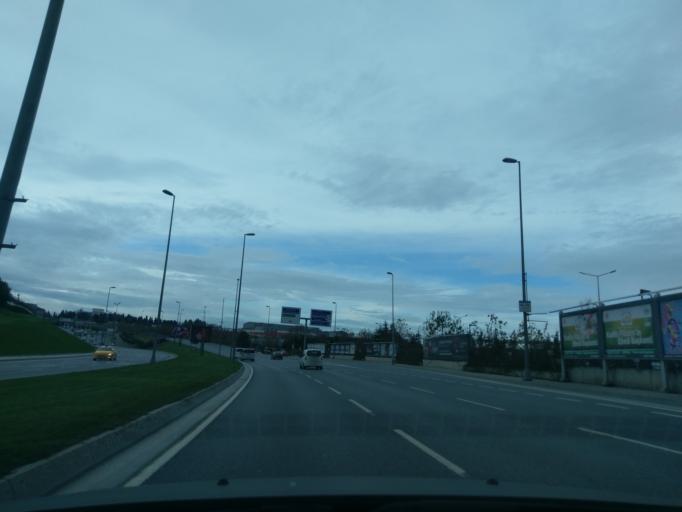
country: TR
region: Istanbul
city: Bahcelievler
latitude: 40.9849
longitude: 28.8304
